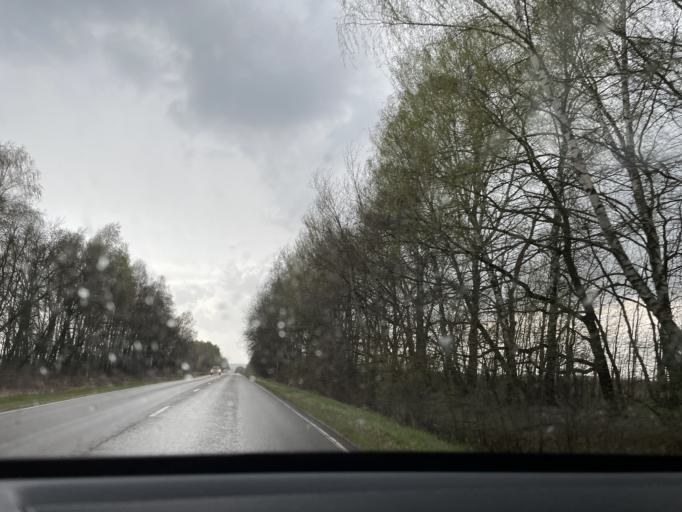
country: RU
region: Tula
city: Novogurovskiy
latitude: 54.5275
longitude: 37.3030
